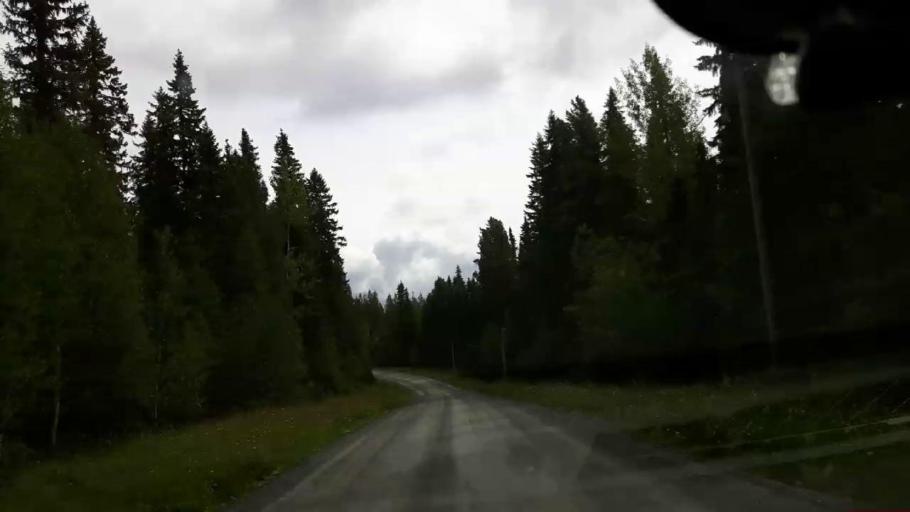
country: SE
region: Jaemtland
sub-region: Krokoms Kommun
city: Valla
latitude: 63.6750
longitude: 13.9377
